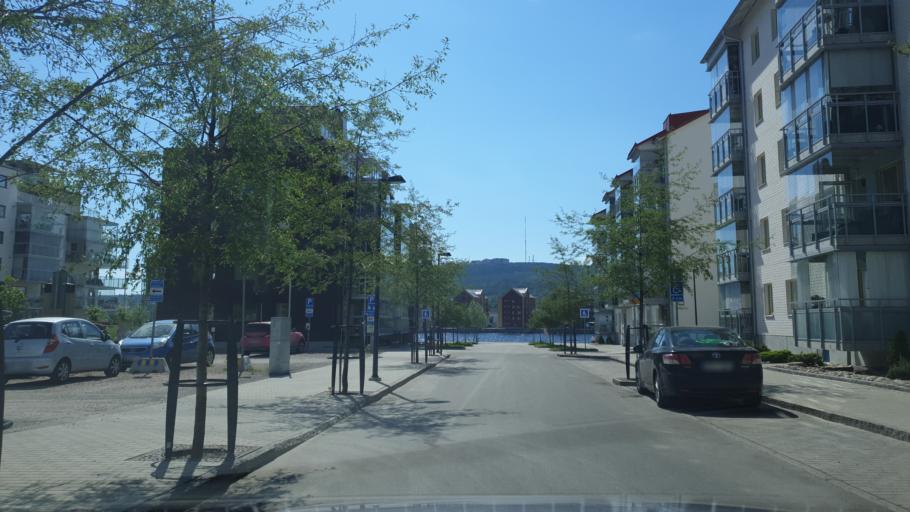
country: SE
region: Vaesternorrland
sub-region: Sundsvalls Kommun
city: Sundsvall
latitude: 62.3941
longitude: 17.3194
